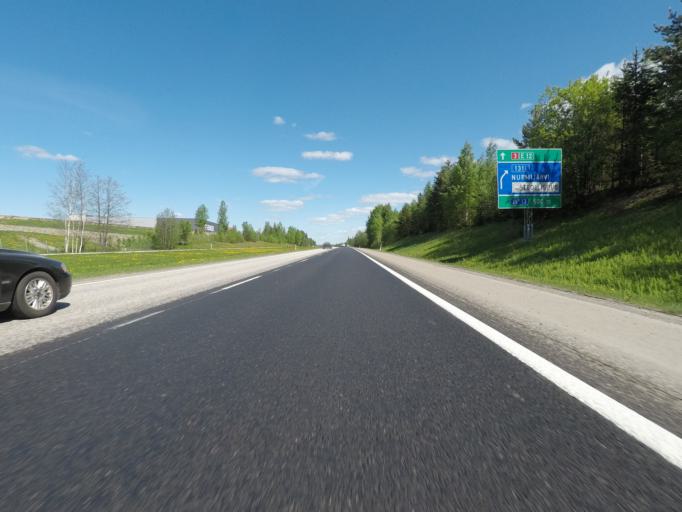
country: FI
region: Uusimaa
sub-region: Helsinki
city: Nurmijaervi
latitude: 60.4459
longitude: 24.8412
